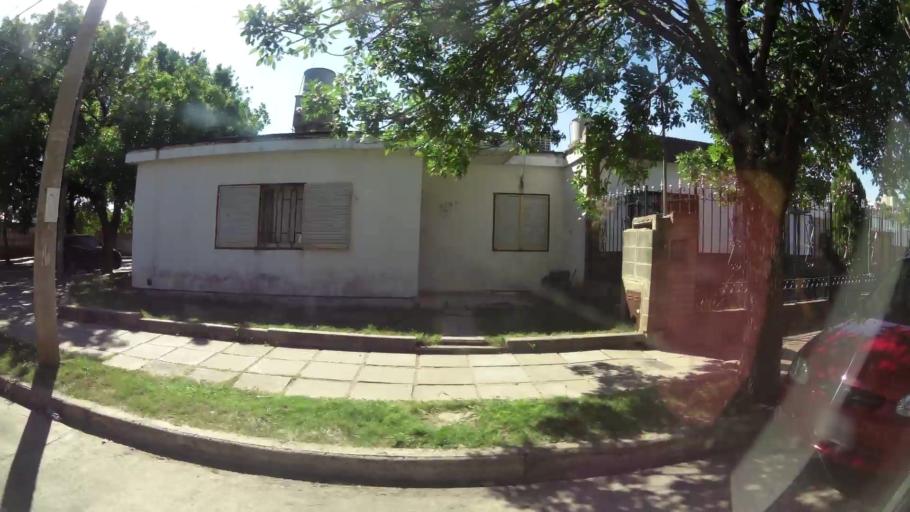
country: AR
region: Cordoba
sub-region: Departamento de Capital
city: Cordoba
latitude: -31.3634
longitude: -64.1675
